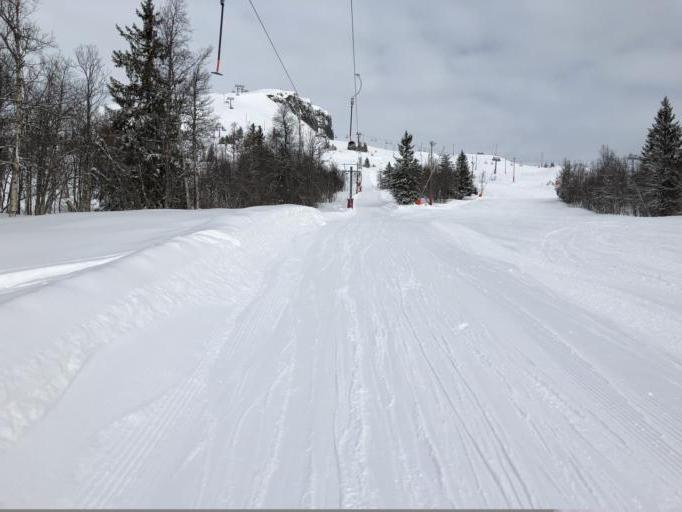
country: NO
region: Oppland
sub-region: Gausdal
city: Segalstad bru
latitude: 61.3405
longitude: 10.0868
